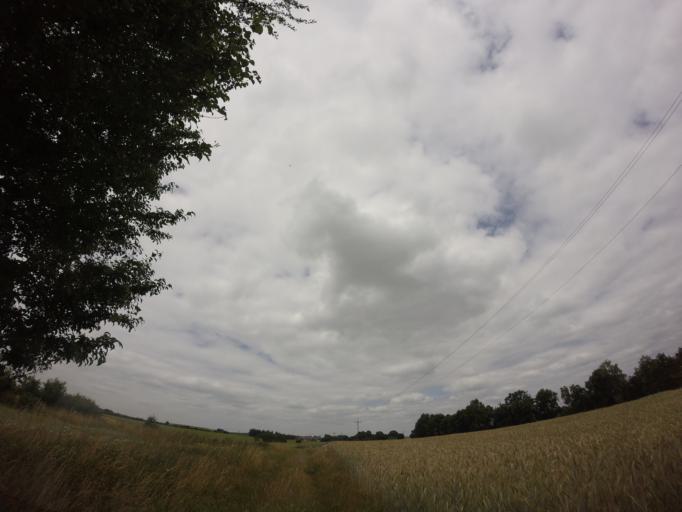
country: PL
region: West Pomeranian Voivodeship
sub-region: Powiat choszczenski
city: Krzecin
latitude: 53.0692
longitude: 15.5299
